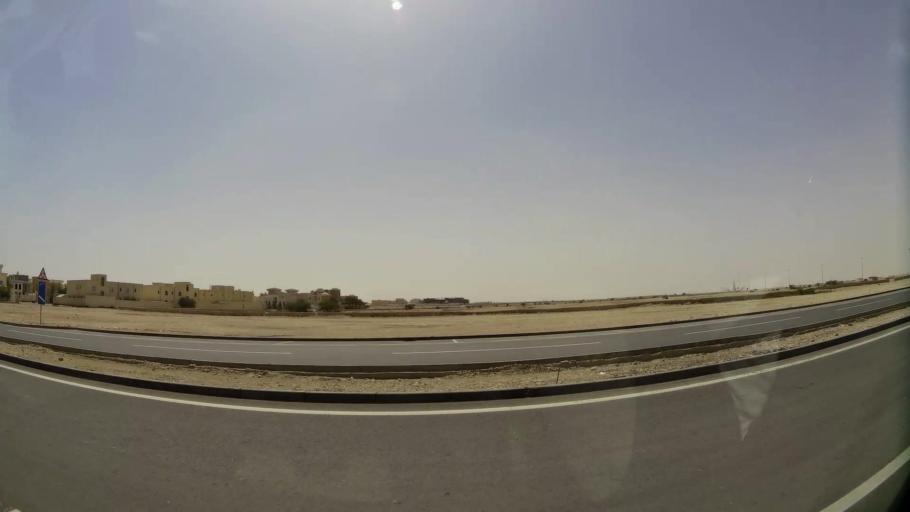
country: QA
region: Baladiyat Umm Salal
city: Umm Salal Muhammad
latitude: 25.3678
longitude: 51.4243
